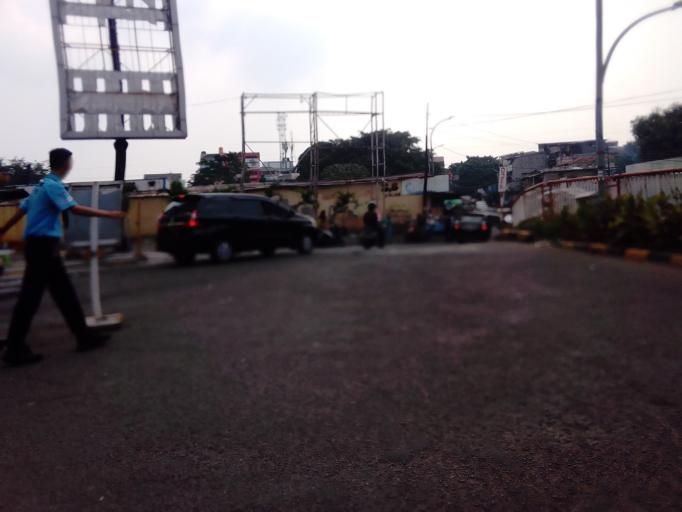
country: ID
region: Jakarta Raya
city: Jakarta
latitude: -6.1938
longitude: 106.8158
